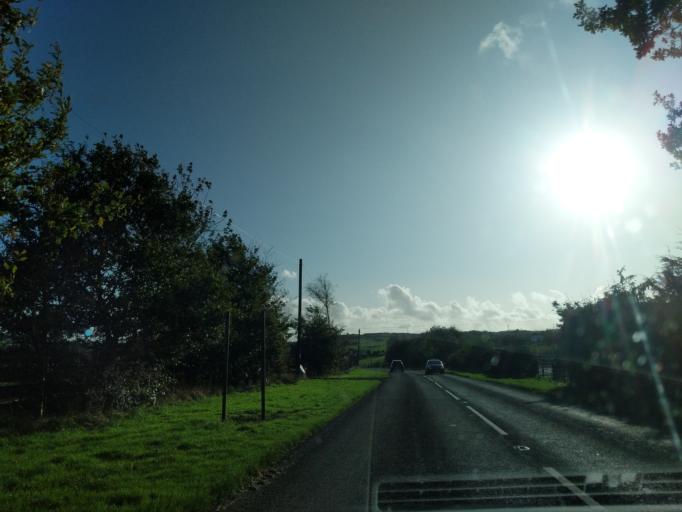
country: GB
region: Scotland
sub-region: Dumfries and Galloway
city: Kirkcudbright
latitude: 54.8816
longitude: -4.0231
